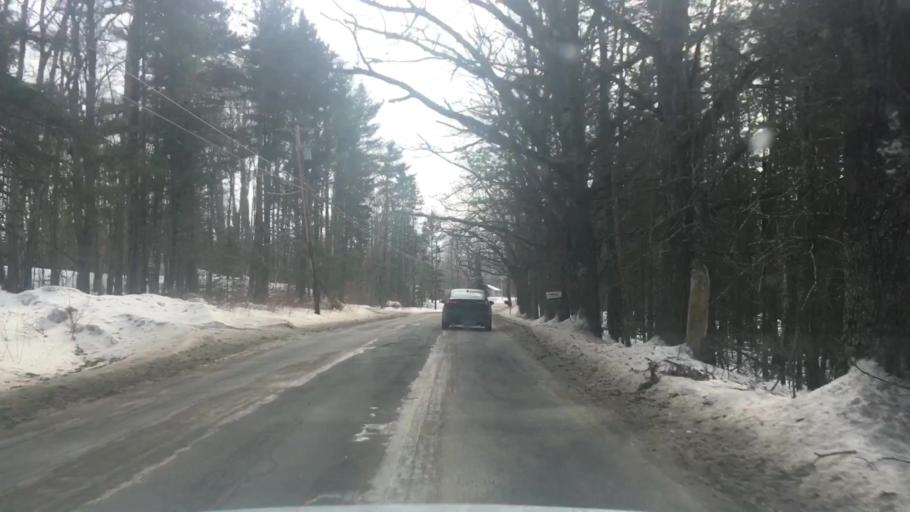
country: US
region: Maine
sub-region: Hancock County
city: Orland
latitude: 44.5827
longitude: -68.7253
